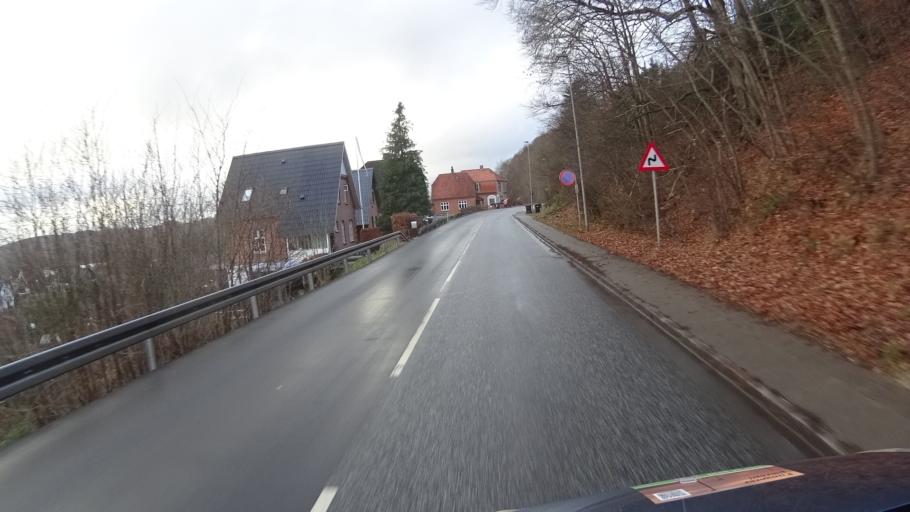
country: DK
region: South Denmark
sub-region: Vejle Kommune
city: Vejle
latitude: 55.7146
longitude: 9.5028
